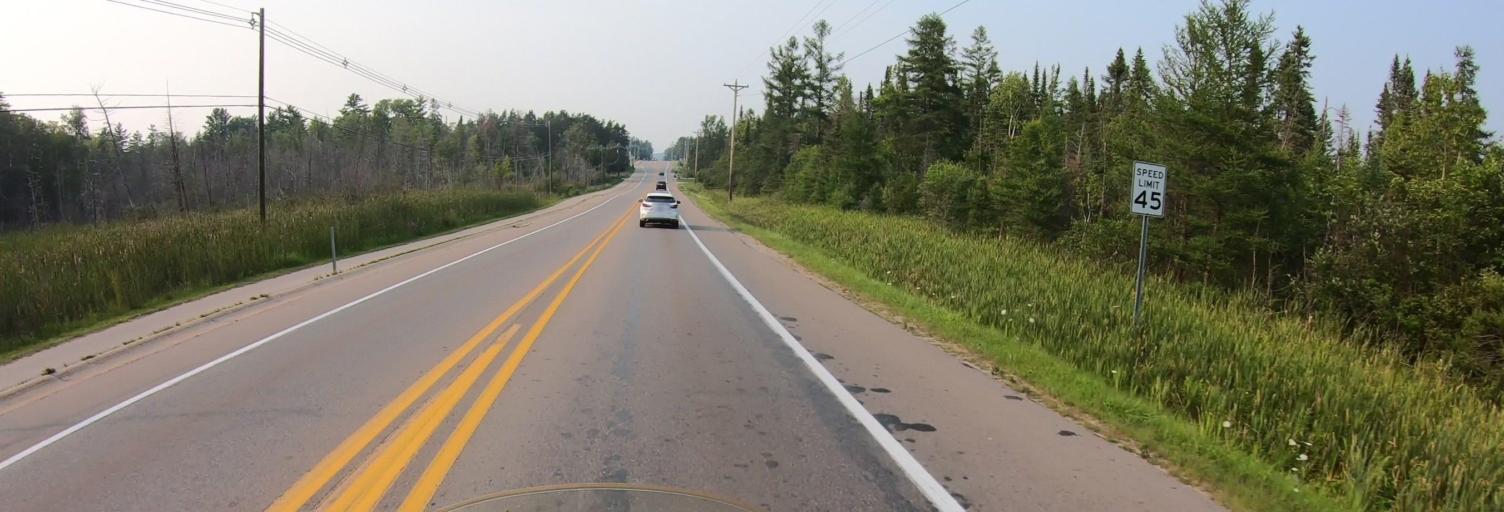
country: US
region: Michigan
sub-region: Emmet County
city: Petoskey
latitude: 45.4158
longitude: -84.9044
